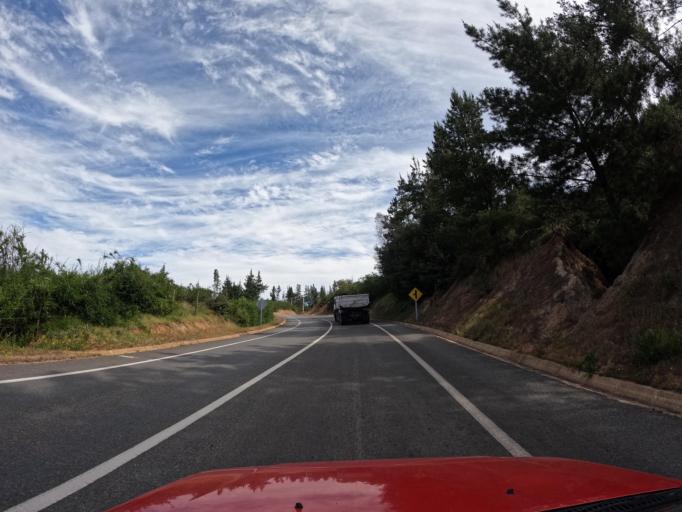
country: CL
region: Maule
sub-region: Provincia de Talca
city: Talca
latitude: -35.1652
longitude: -71.9727
